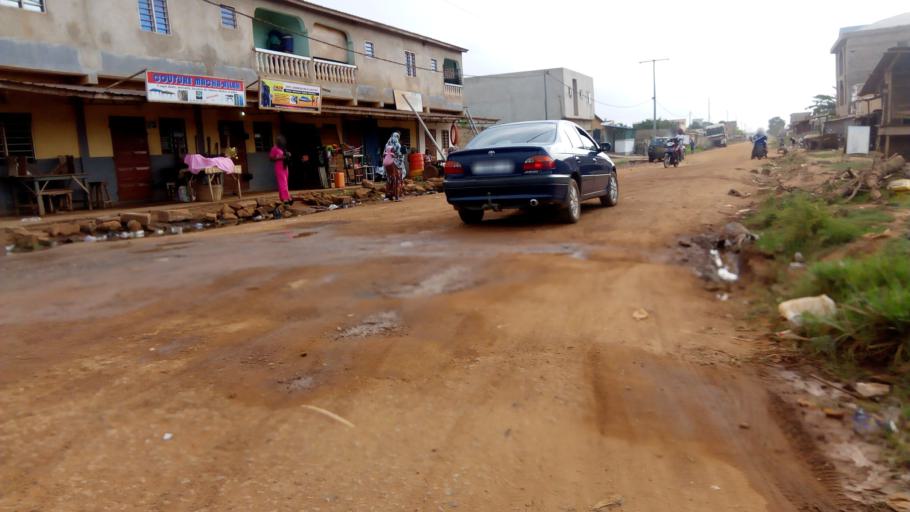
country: TG
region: Maritime
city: Lome
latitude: 6.2521
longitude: 1.2159
